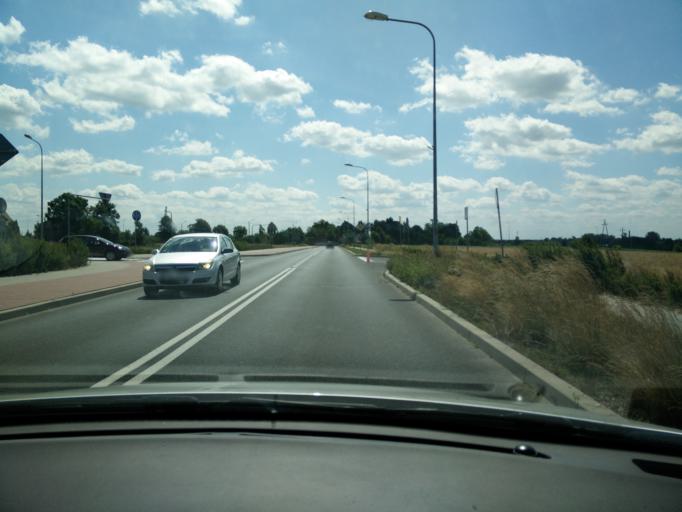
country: PL
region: Greater Poland Voivodeship
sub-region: Powiat sredzki
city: Sroda Wielkopolska
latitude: 52.2339
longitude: 17.2963
